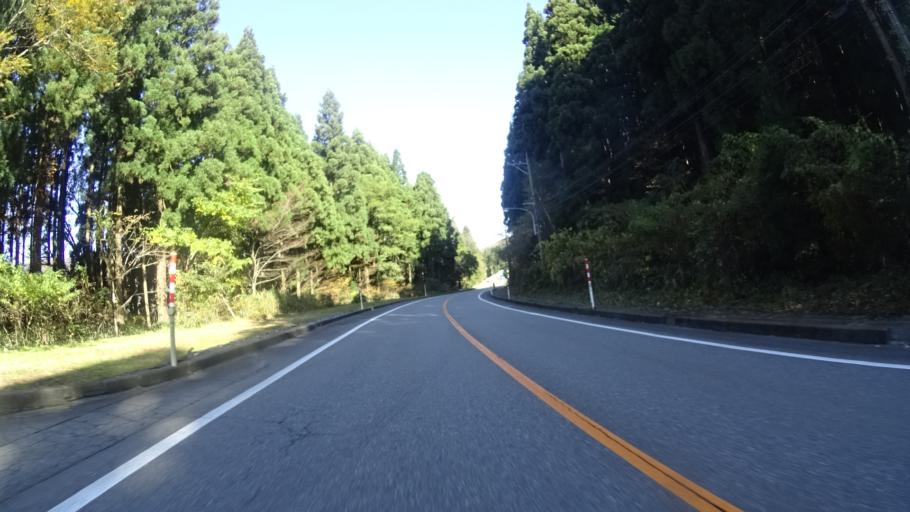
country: JP
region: Ishikawa
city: Tsurugi-asahimachi
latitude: 36.3712
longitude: 136.6137
